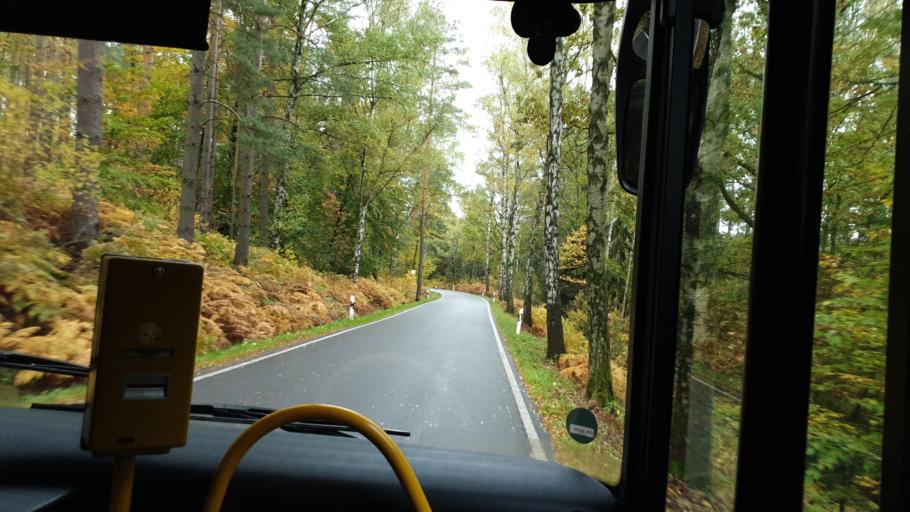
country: DE
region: Saxony
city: Kurort Gohrisch
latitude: 50.8909
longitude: 14.1013
